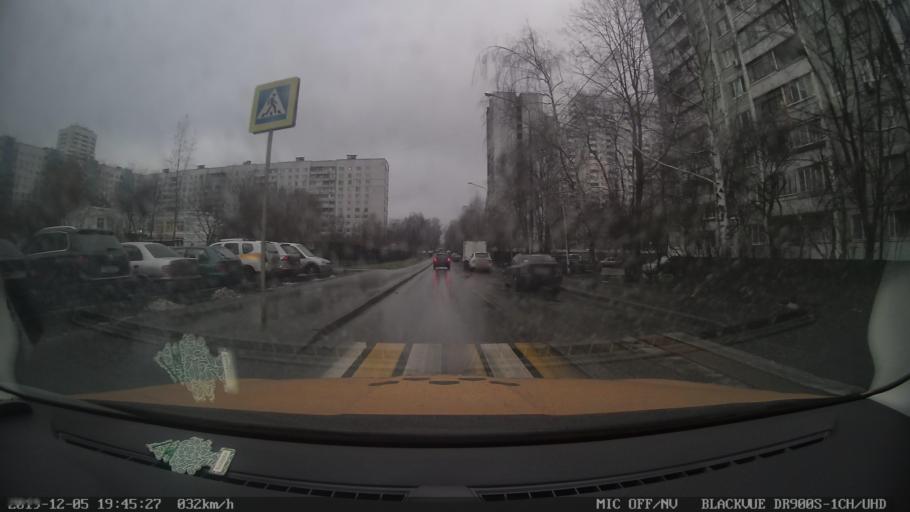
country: RU
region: Moscow
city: Lianozovo
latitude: 55.9038
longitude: 37.5775
